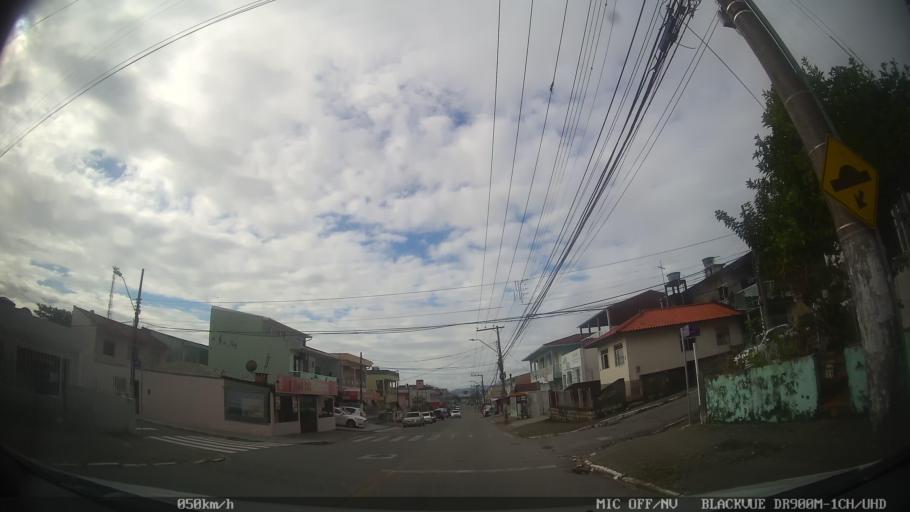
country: BR
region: Santa Catarina
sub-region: Sao Jose
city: Campinas
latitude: -27.5704
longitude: -48.6174
